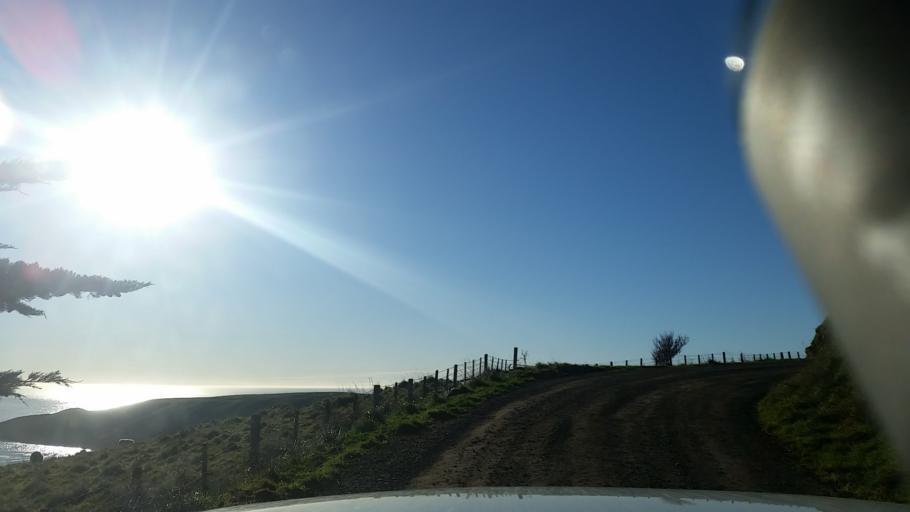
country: NZ
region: Canterbury
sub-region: Christchurch City
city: Christchurch
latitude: -43.6985
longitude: 173.0679
